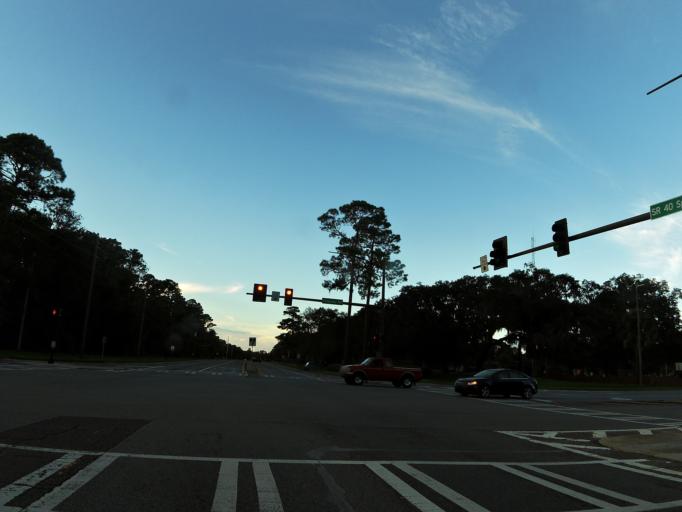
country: US
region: Georgia
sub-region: Camden County
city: Kings Bay Base
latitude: 30.7917
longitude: -81.5769
